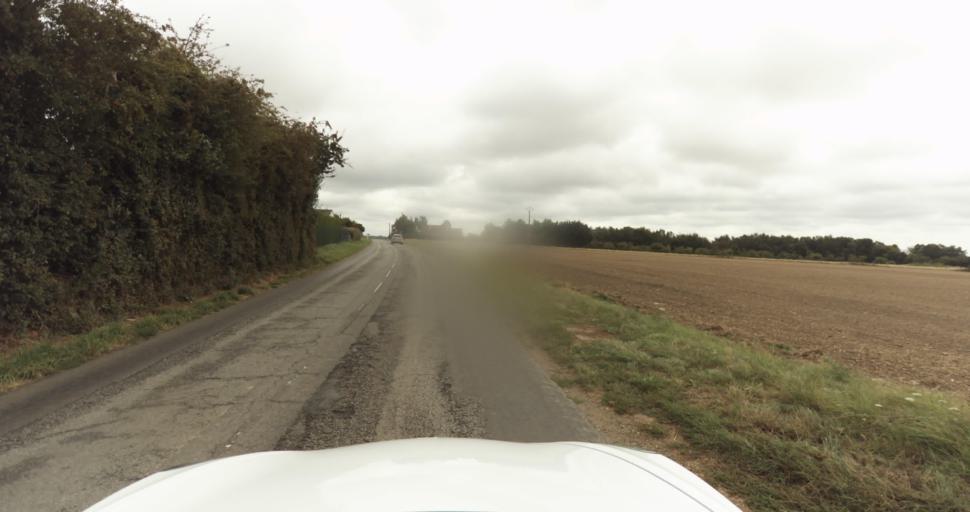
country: FR
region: Haute-Normandie
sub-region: Departement de l'Eure
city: Aviron
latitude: 49.0644
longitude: 1.0714
